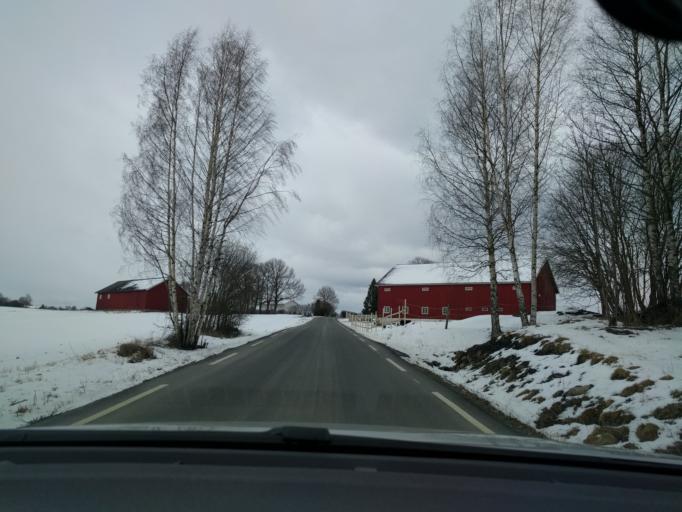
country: NO
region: Hedmark
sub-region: Stange
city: Stange
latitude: 60.6918
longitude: 11.1405
